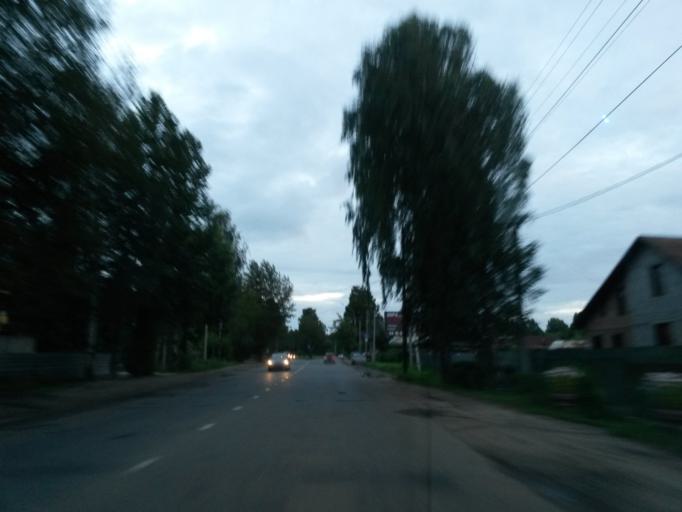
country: RU
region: Jaroslavl
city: Yaroslavl
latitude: 57.6489
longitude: 39.9077
